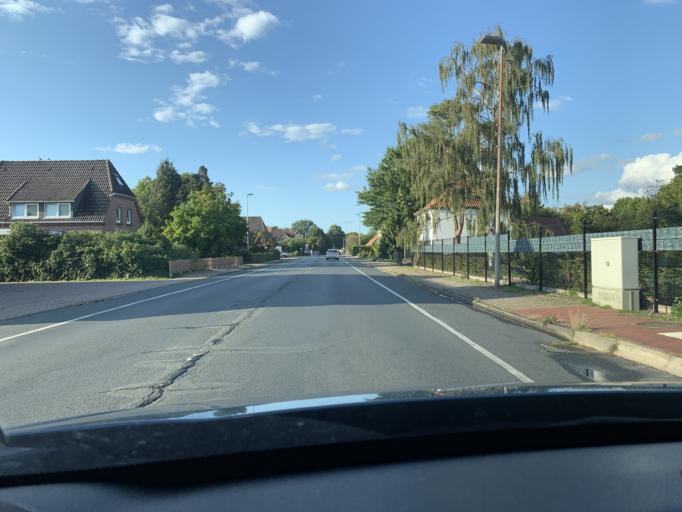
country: DE
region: Lower Saxony
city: Edewecht
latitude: 53.1338
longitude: 7.9867
